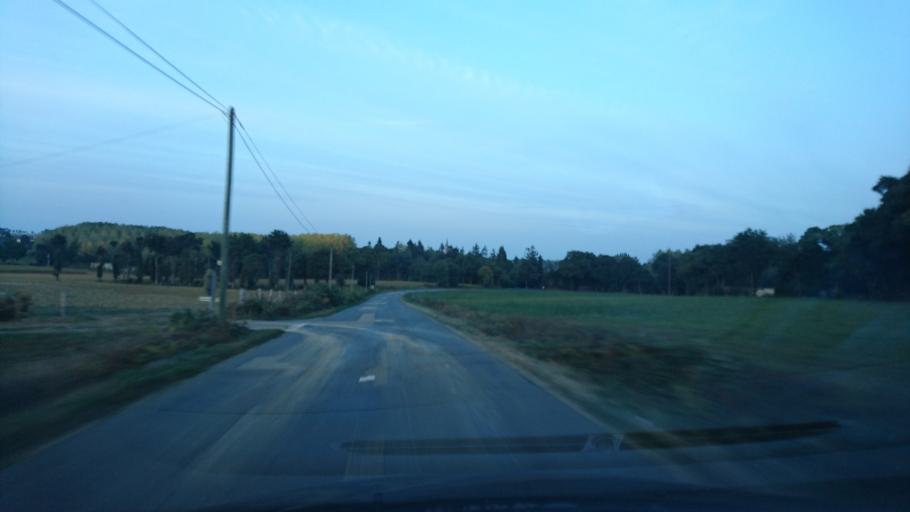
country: FR
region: Brittany
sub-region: Departement d'Ille-et-Vilaine
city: Guignen
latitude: 47.9144
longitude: -1.8721
